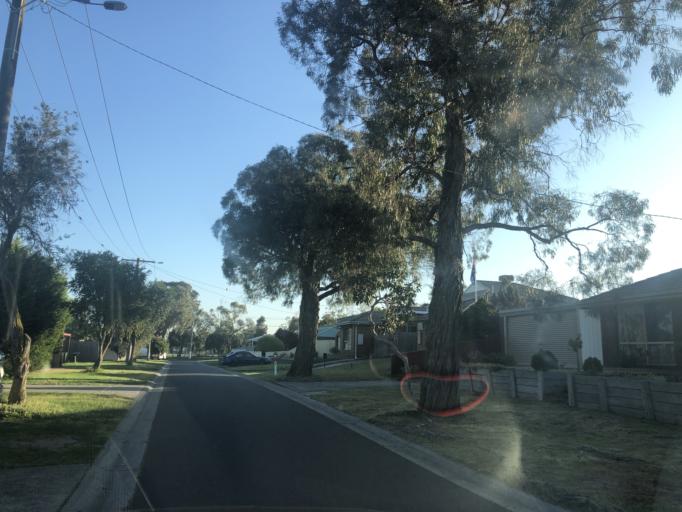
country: AU
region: Victoria
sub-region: Casey
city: Hampton Park
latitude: -38.0395
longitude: 145.2571
